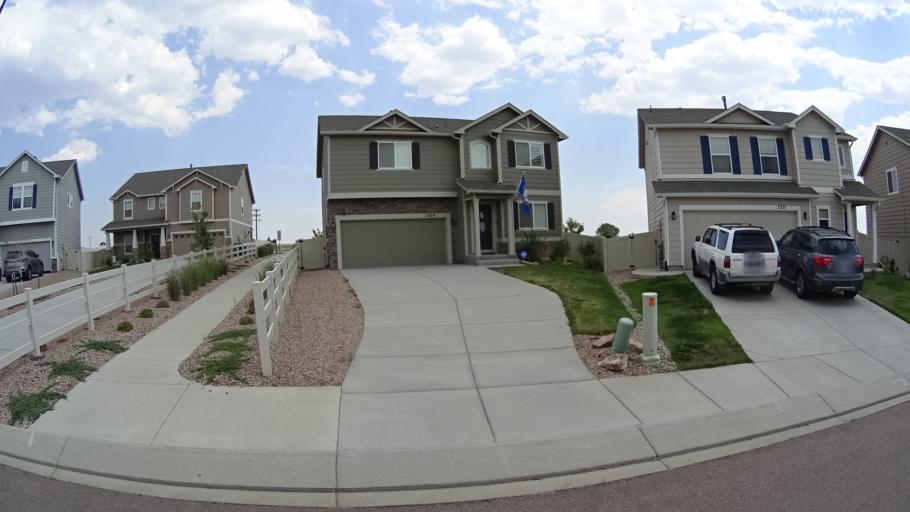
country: US
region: Colorado
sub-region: El Paso County
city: Black Forest
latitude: 38.9545
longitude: -104.6896
